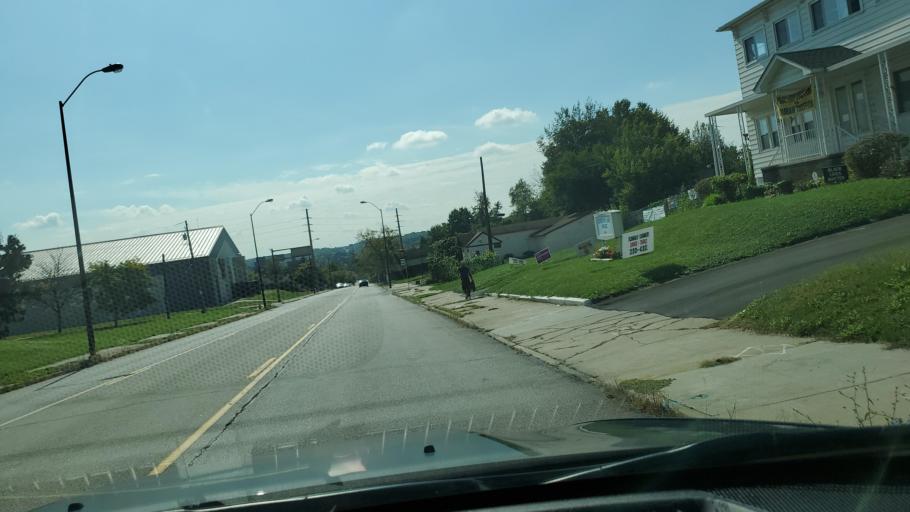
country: US
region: Ohio
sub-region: Mahoning County
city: Youngstown
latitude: 41.1105
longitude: -80.6553
